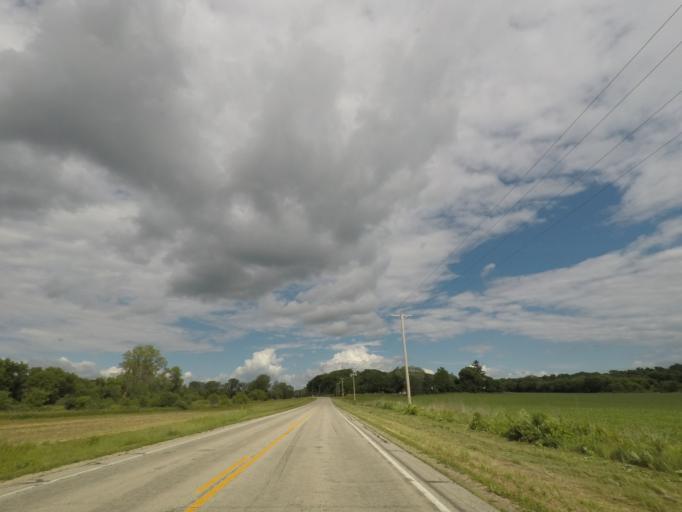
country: US
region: Wisconsin
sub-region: Green County
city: Brooklyn
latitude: 42.8272
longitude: -89.4448
